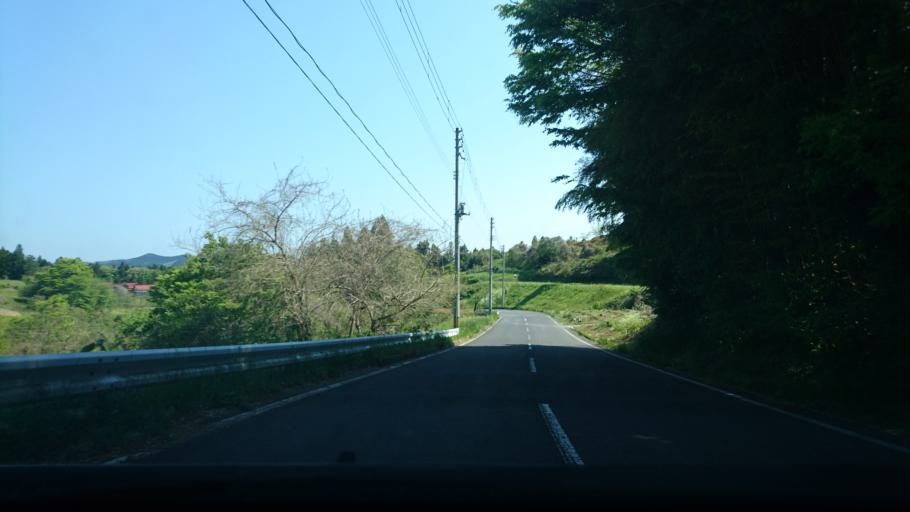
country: JP
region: Iwate
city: Ichinoseki
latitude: 38.9201
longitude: 141.2776
